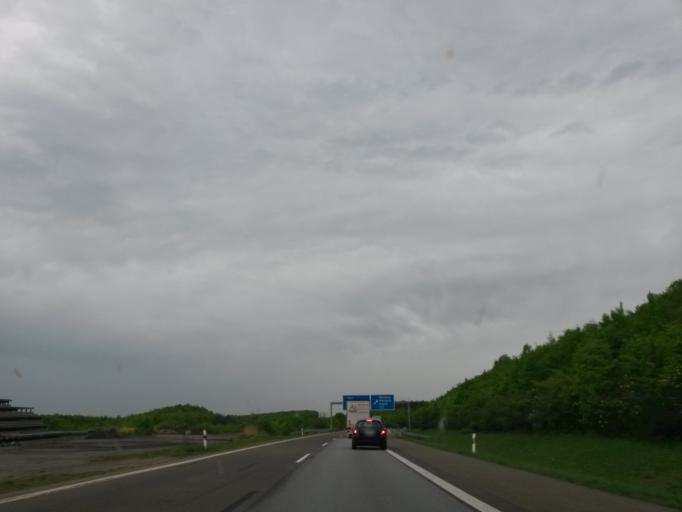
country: DE
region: Bavaria
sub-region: Regierungsbezirk Unterfranken
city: Eisingen
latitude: 49.7405
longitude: 9.8231
